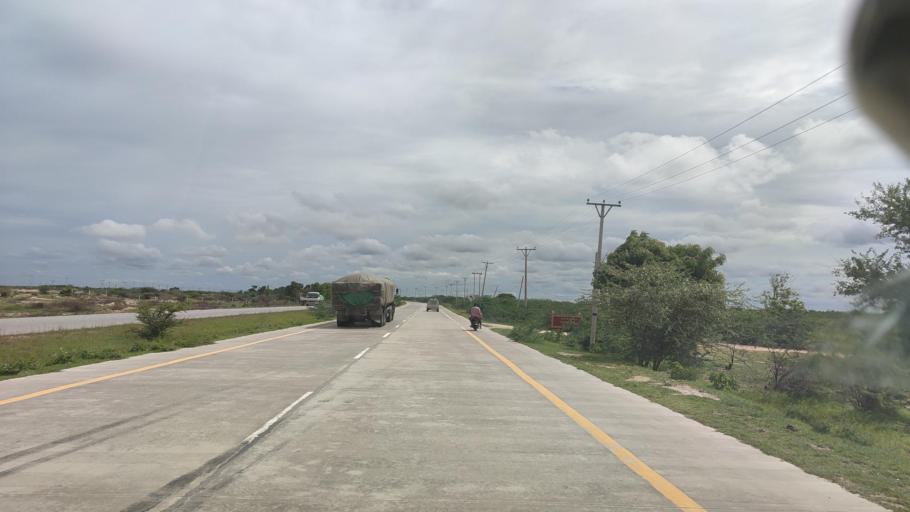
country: MM
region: Mandalay
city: Meiktila
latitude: 21.0392
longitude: 95.9950
